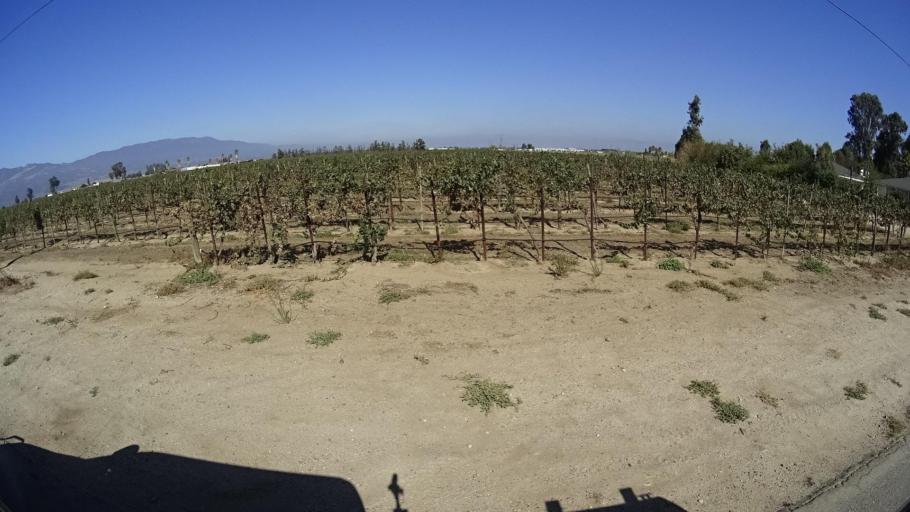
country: US
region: California
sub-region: Monterey County
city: Greenfield
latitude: 36.3137
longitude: -121.2623
